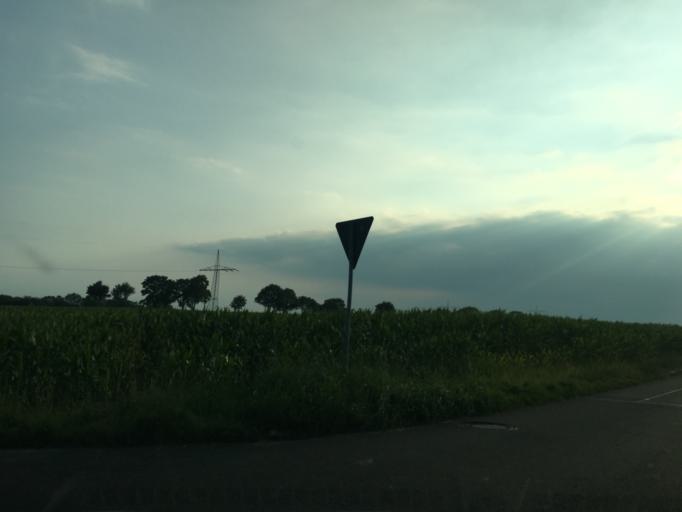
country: DE
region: North Rhine-Westphalia
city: Huckelhoven
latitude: 51.0685
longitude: 6.2464
